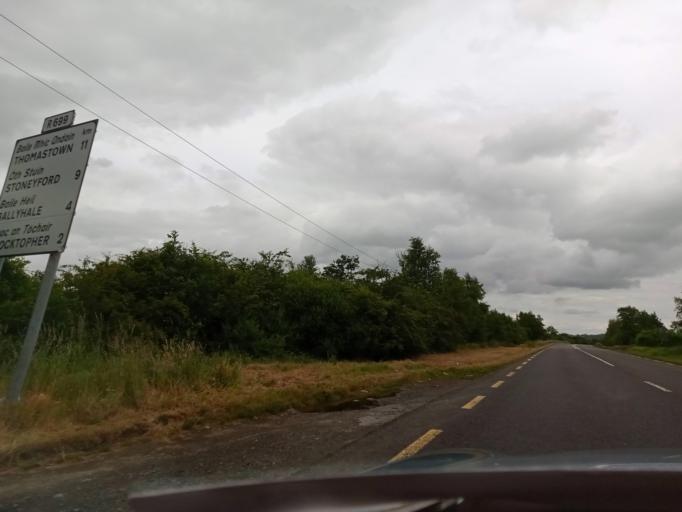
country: IE
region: Leinster
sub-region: Kilkenny
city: Thomastown
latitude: 52.4862
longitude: -7.2360
